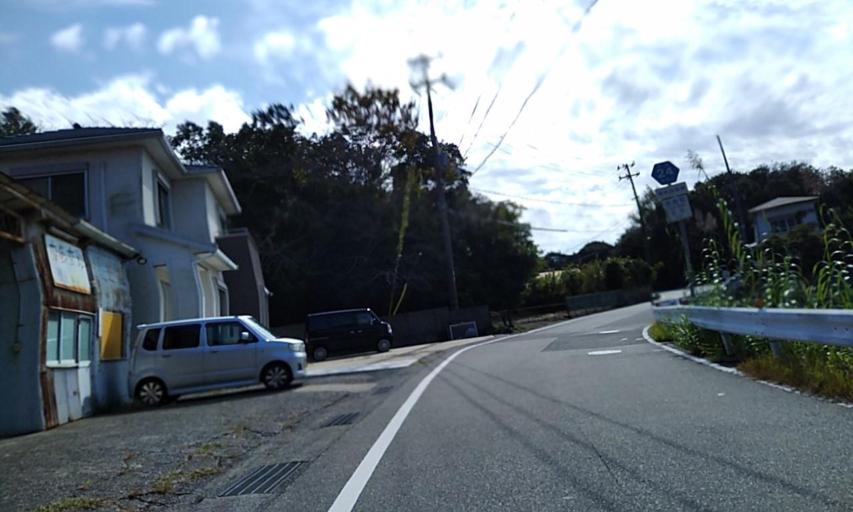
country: JP
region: Wakayama
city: Gobo
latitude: 33.9673
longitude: 135.1029
